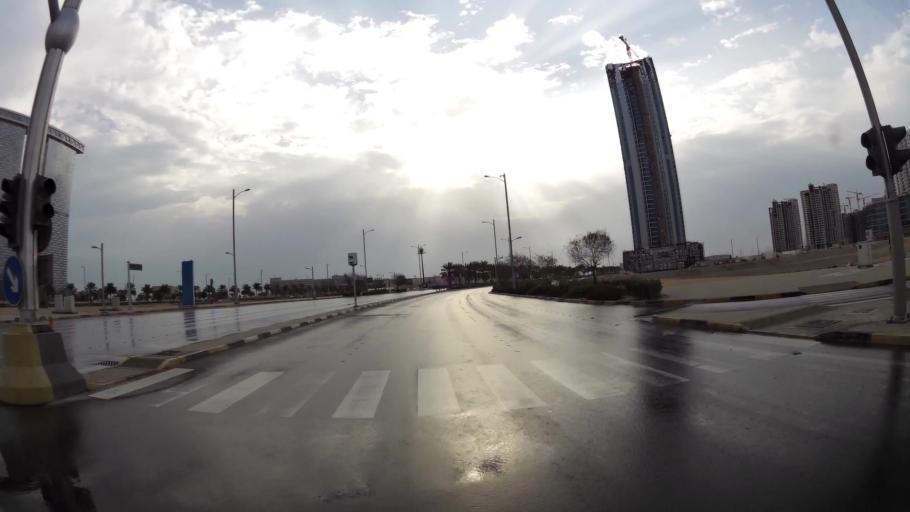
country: AE
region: Abu Dhabi
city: Abu Dhabi
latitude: 24.4899
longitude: 54.4032
